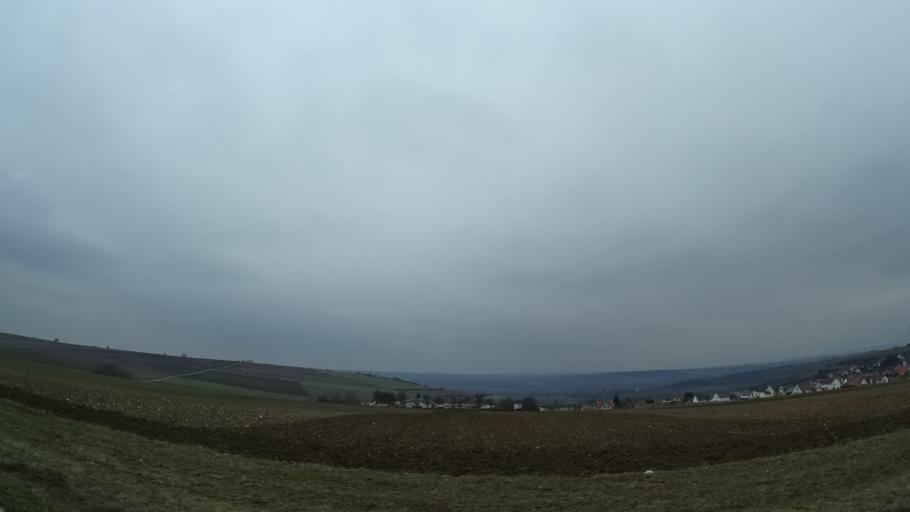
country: DE
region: Rheinland-Pfalz
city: Stetten
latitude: 49.6764
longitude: 8.0975
